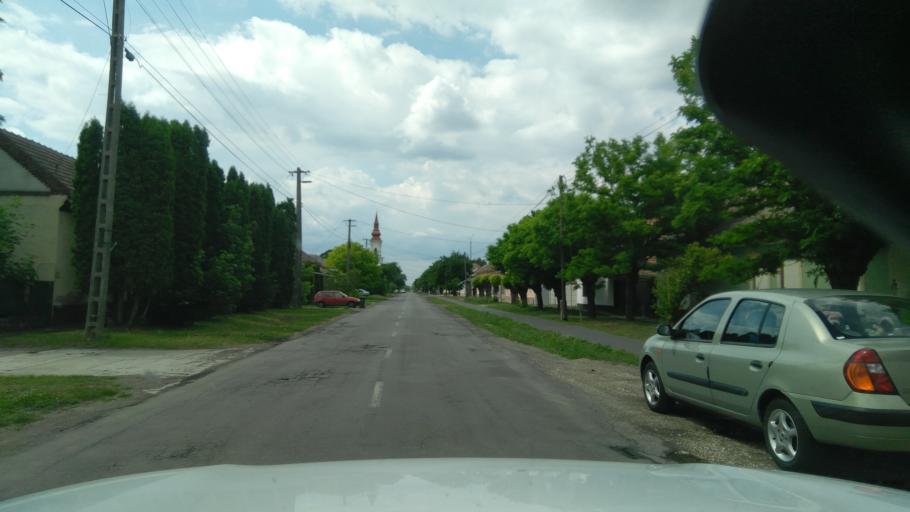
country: HU
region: Bekes
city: Magyarbanhegyes
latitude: 46.4543
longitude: 20.9683
